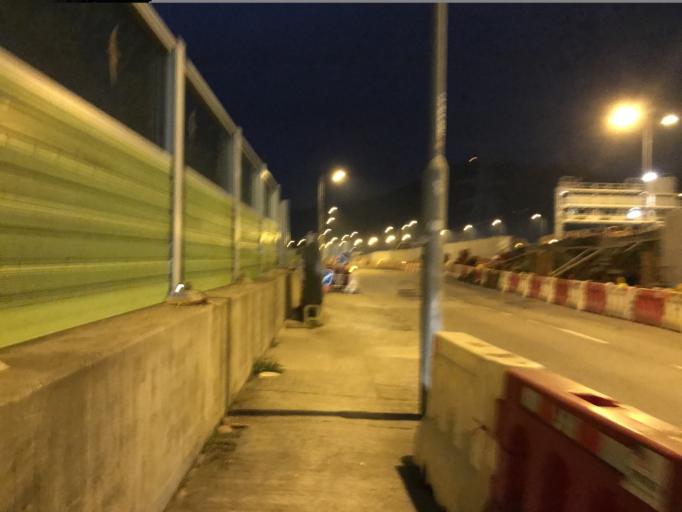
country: HK
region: Tai Po
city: Tai Po
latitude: 22.4653
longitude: 114.1496
